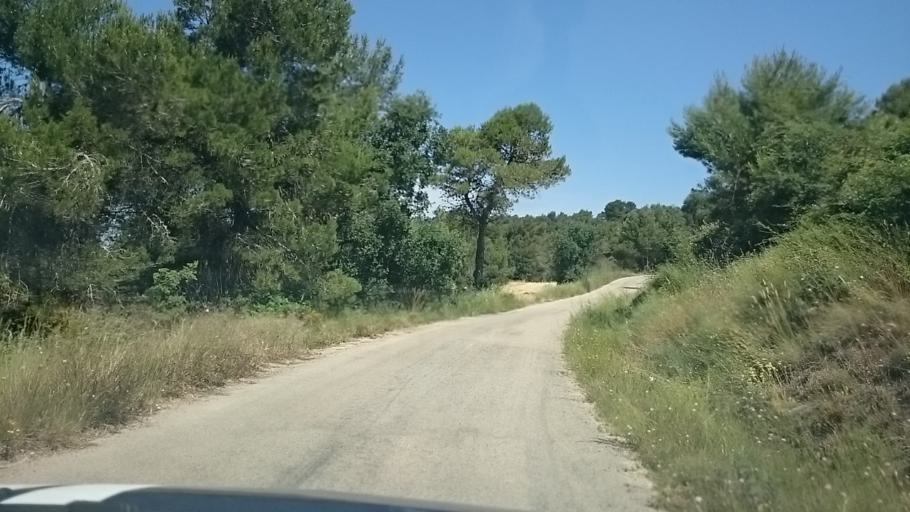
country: ES
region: Catalonia
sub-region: Provincia de Tarragona
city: Querol
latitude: 41.4030
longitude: 1.4176
